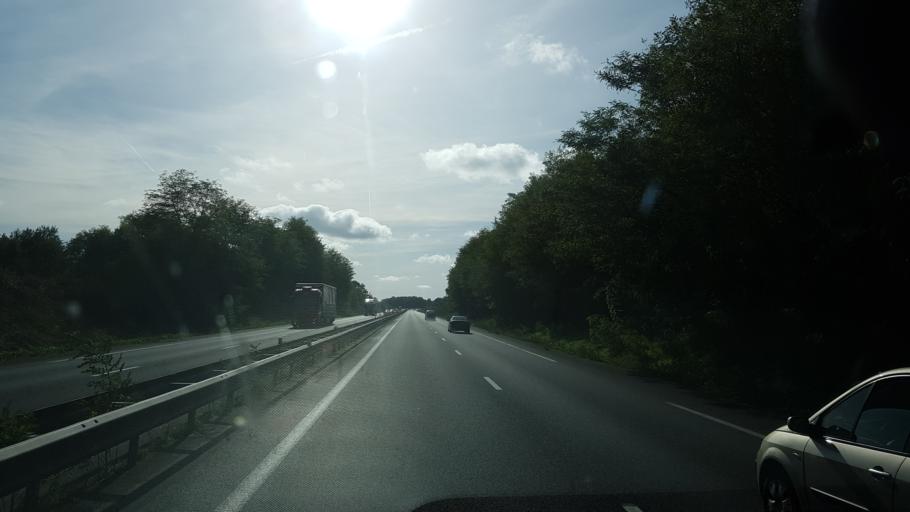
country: FR
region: Poitou-Charentes
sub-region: Departement de la Charente
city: Chasseneuil-sur-Bonnieure
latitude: 45.8021
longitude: 0.4393
